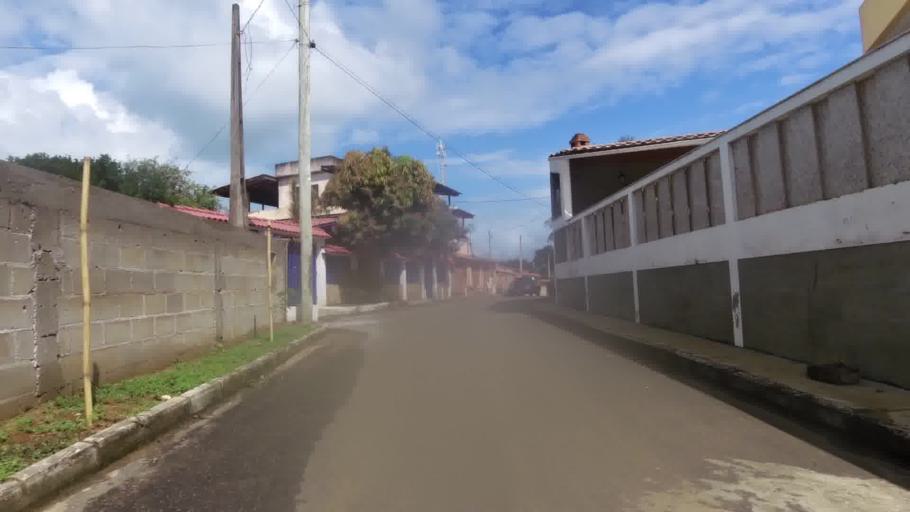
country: BR
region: Espirito Santo
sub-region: Piuma
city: Piuma
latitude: -20.8268
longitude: -40.6937
